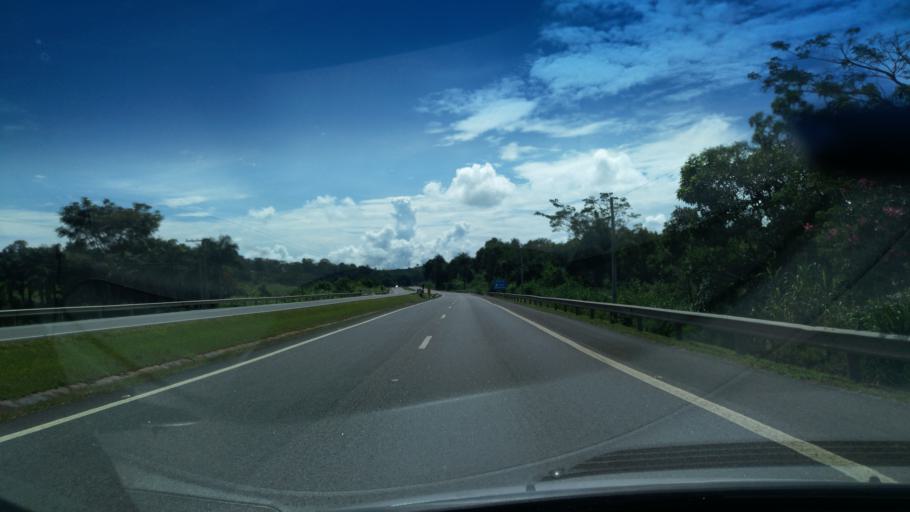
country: BR
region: Sao Paulo
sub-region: Santo Antonio Do Jardim
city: Espirito Santo do Pinhal
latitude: -22.2319
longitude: -46.7963
